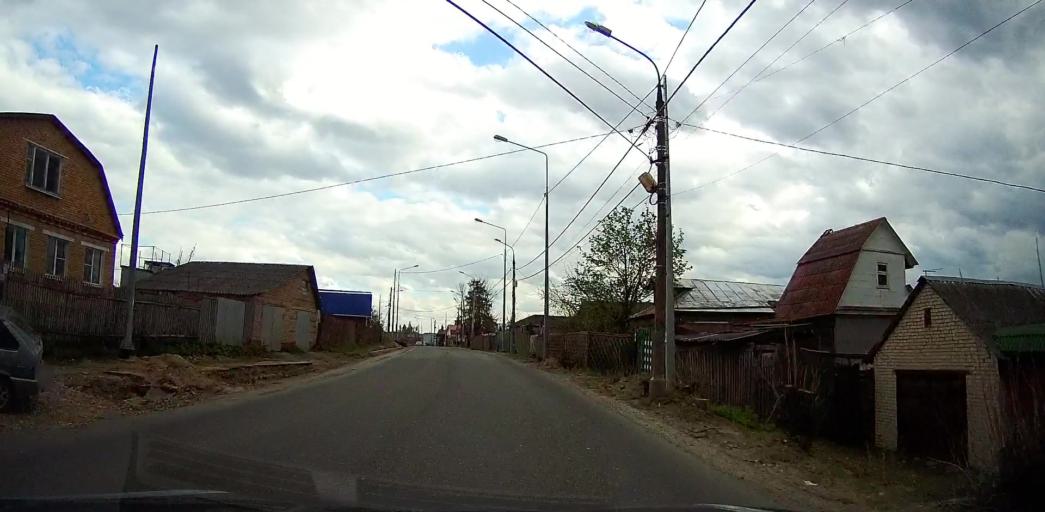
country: RU
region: Moskovskaya
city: Pavlovskiy Posad
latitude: 55.7906
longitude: 38.6849
